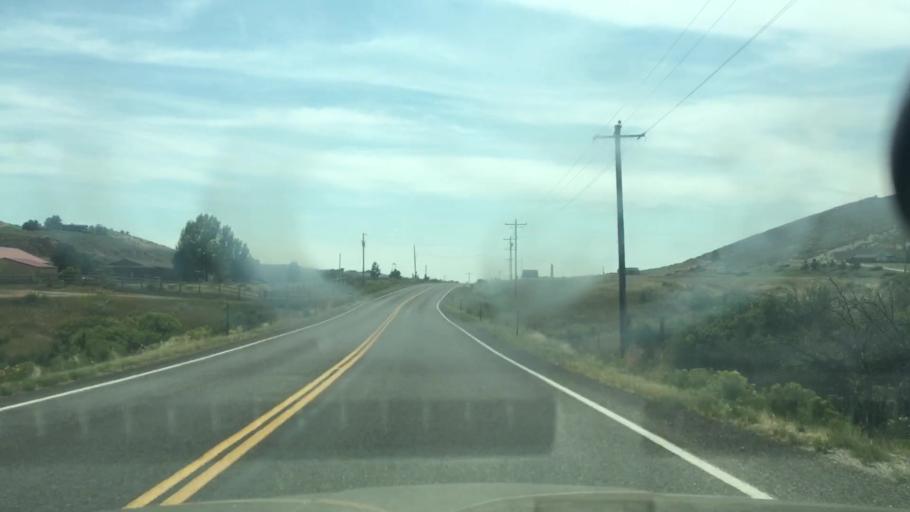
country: US
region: Colorado
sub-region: Larimer County
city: Campion
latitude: 40.3657
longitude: -105.1887
